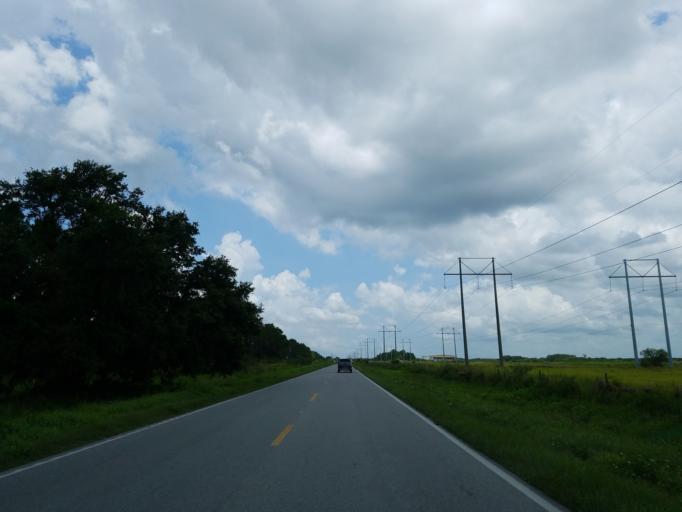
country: US
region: Florida
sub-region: Polk County
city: Willow Oak
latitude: 27.8507
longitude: -82.0434
